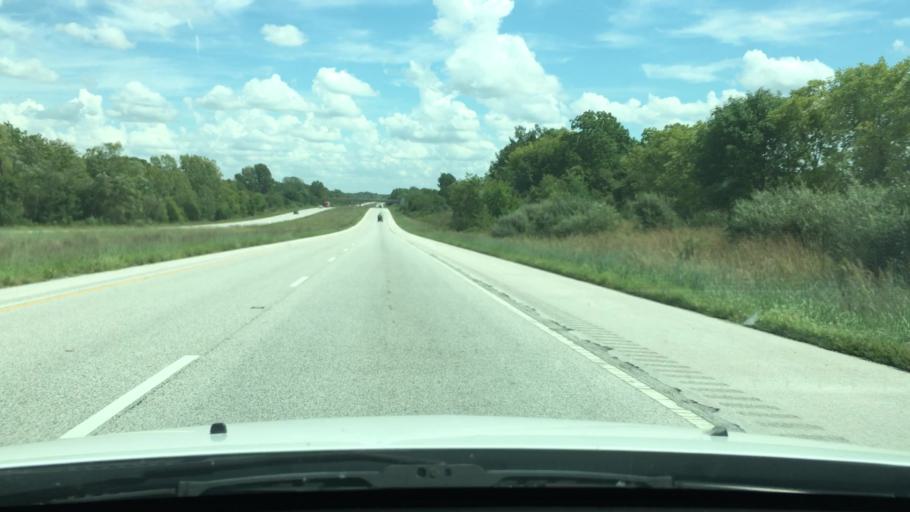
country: US
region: Illinois
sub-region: Scott County
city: Winchester
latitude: 39.6812
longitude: -90.4245
